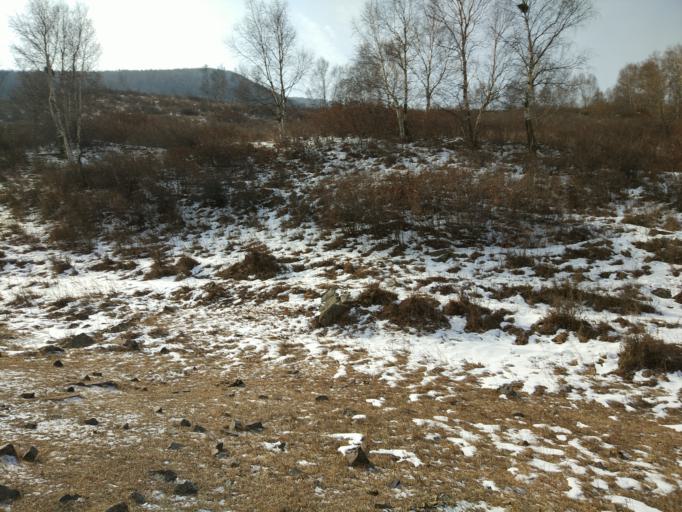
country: CN
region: Hebei
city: Xiwanzi
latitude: 40.8556
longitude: 115.4576
